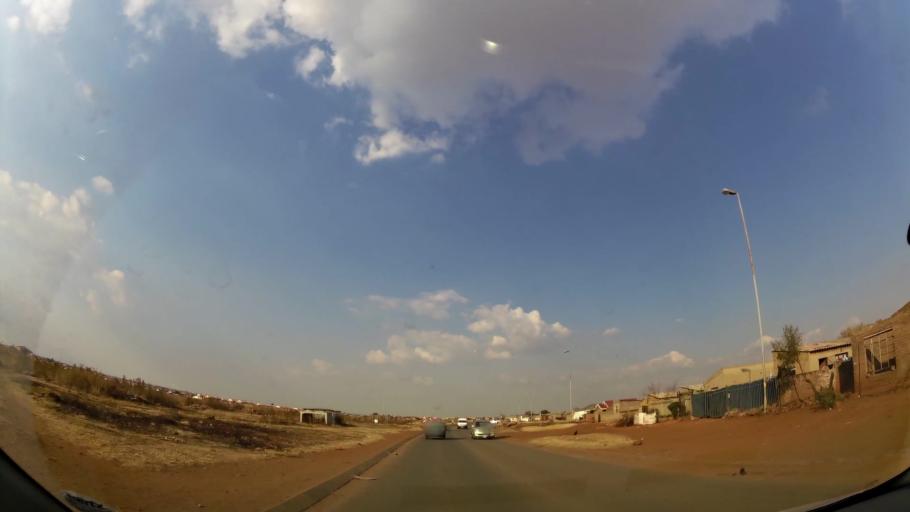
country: ZA
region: Gauteng
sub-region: Ekurhuleni Metropolitan Municipality
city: Germiston
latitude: -26.3701
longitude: 28.1971
